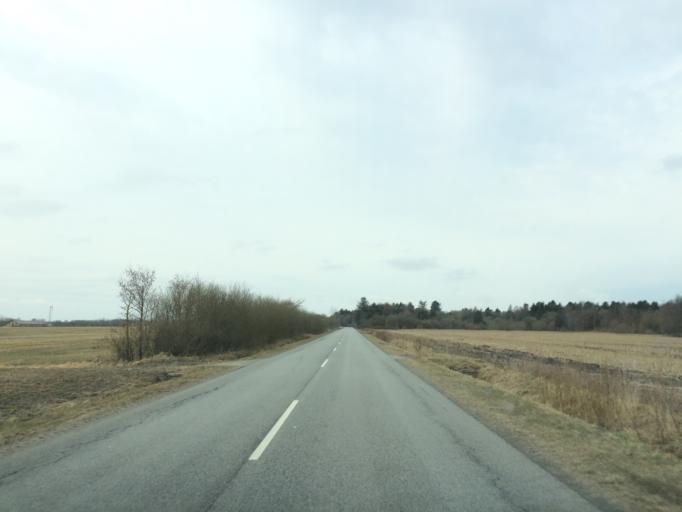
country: DK
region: Central Jutland
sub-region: Ringkobing-Skjern Kommune
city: Tarm
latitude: 55.8305
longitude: 8.4431
